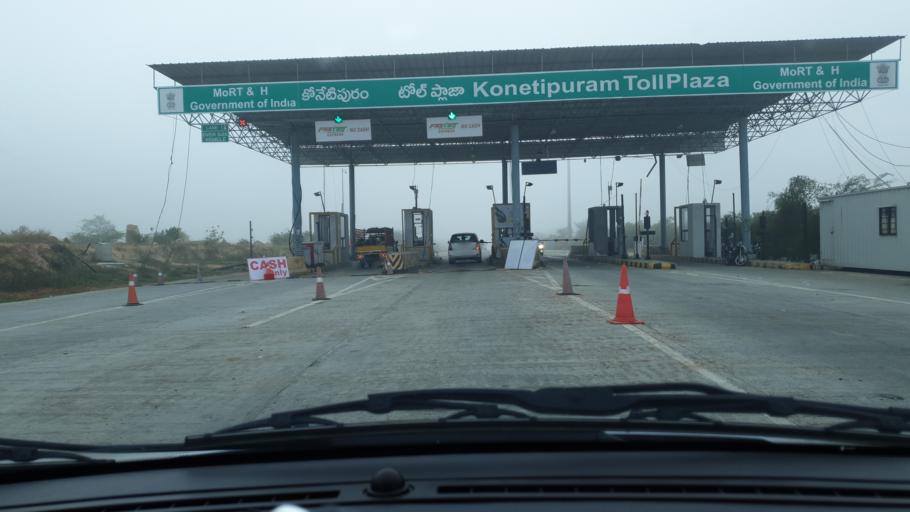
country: IN
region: Telangana
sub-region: Nalgonda
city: Devarkonda
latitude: 16.6124
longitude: 78.6758
